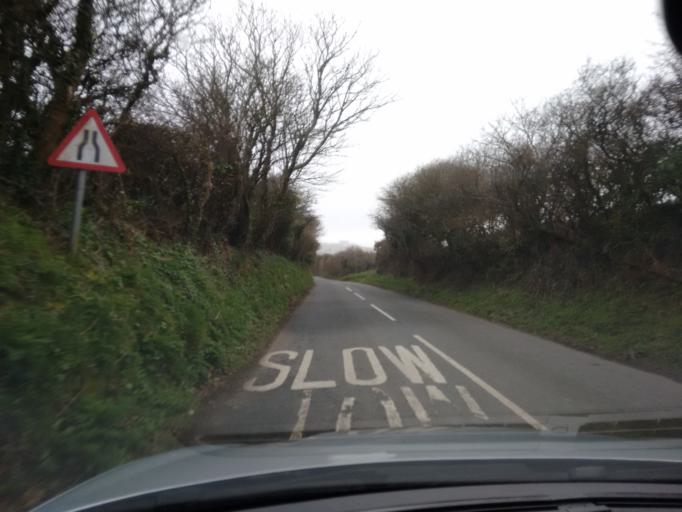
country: GB
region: England
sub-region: Cornwall
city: Tintagel
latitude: 50.6626
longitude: -4.7252
